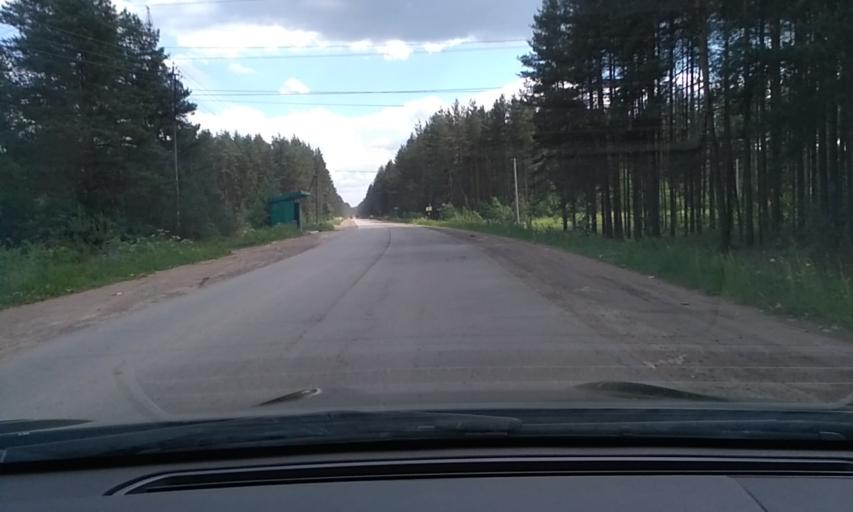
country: RU
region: Leningrad
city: Imeni Sverdlova
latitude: 59.8562
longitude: 30.6734
